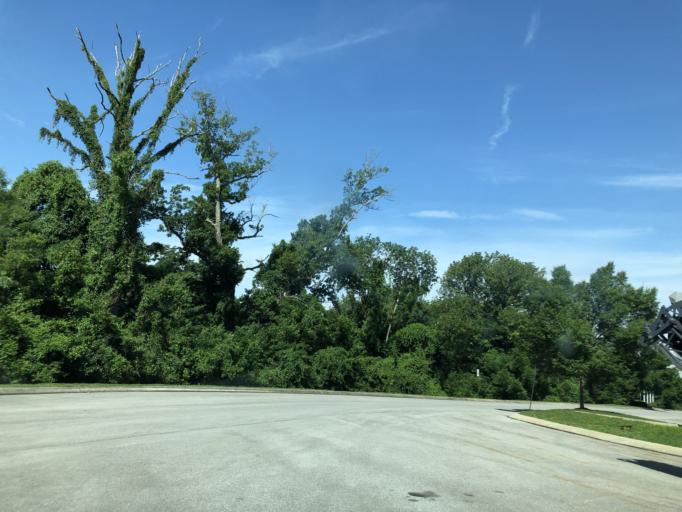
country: US
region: Tennessee
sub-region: Rutherford County
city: La Vergne
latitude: 36.0339
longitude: -86.6299
